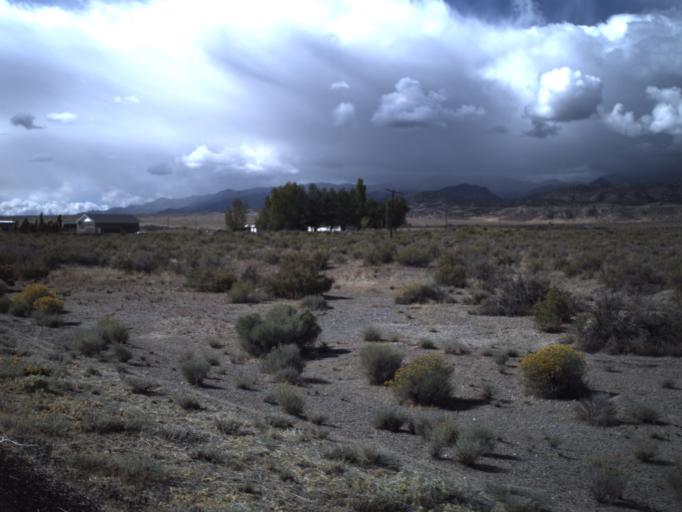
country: US
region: Nevada
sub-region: White Pine County
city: McGill
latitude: 38.9427
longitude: -114.0334
